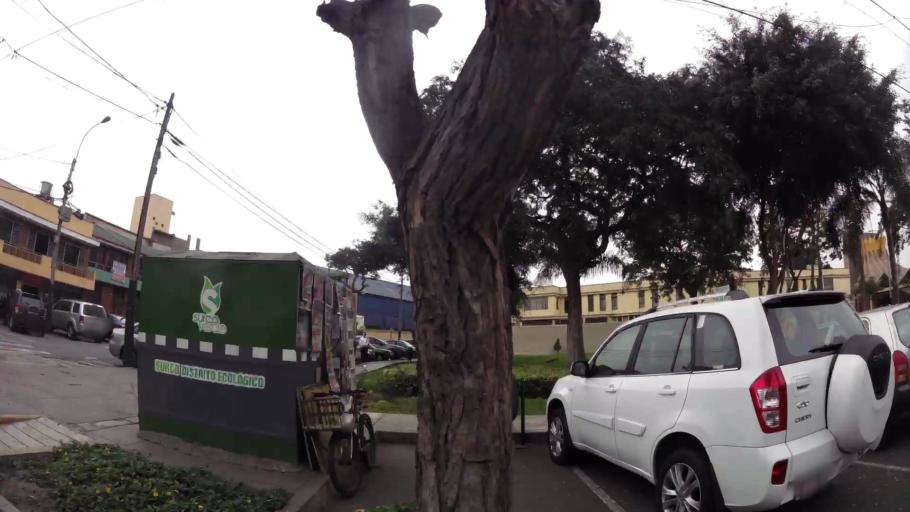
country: PE
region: Lima
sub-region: Lima
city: Surco
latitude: -12.1277
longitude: -76.9960
